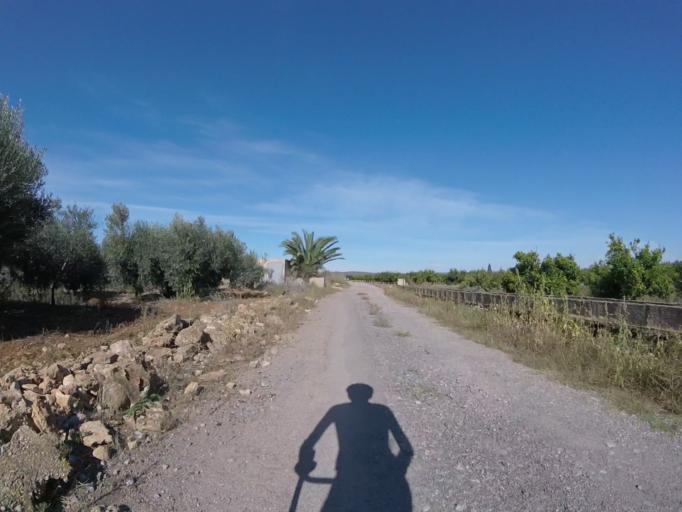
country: ES
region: Valencia
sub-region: Provincia de Castello
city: Torreblanca
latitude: 40.2086
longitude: 0.2347
